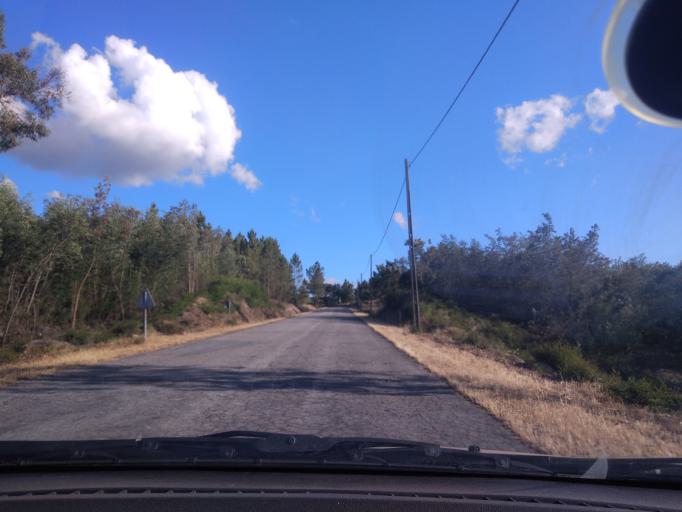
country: PT
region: Castelo Branco
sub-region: Covilha
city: Teixoso
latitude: 40.2422
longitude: -7.3858
